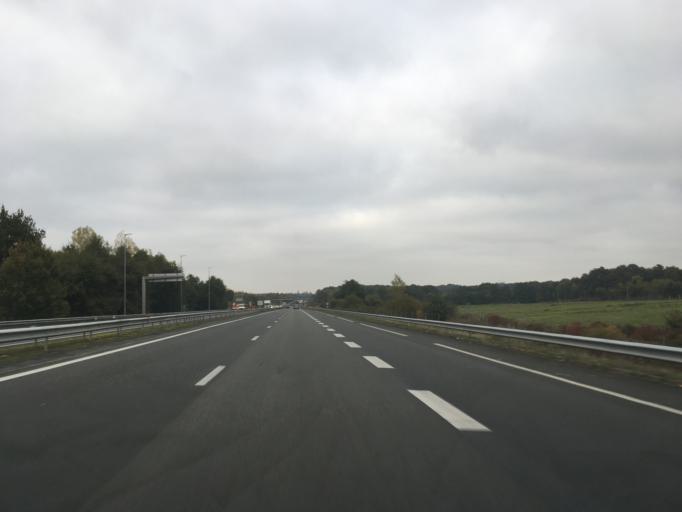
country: FR
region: Pays de la Loire
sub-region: Departement de la Sarthe
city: Parce-sur-Sarthe
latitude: 47.8089
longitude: -0.1642
